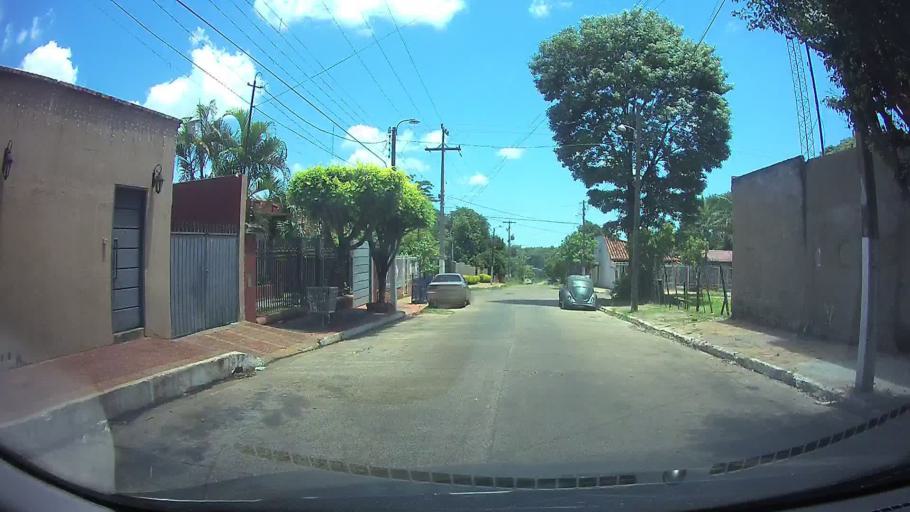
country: PY
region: Central
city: San Lorenzo
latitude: -25.2584
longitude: -57.4861
